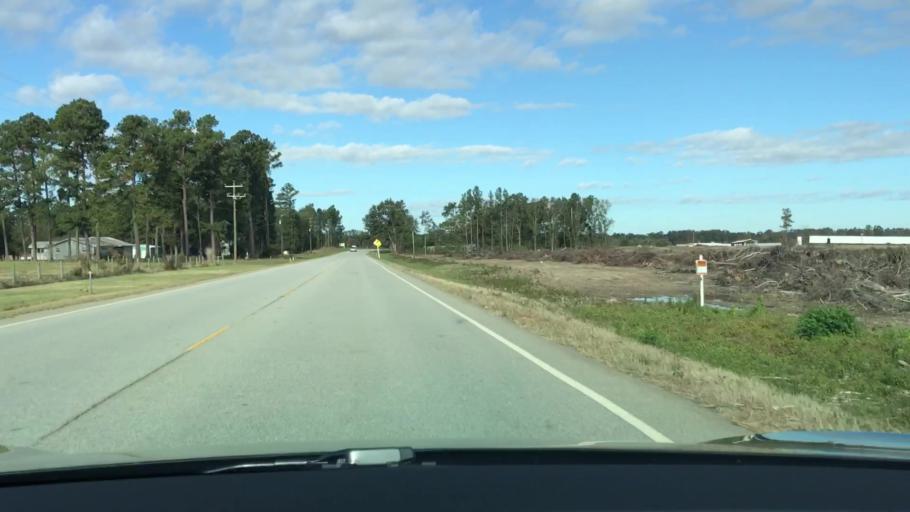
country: US
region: Georgia
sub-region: Jefferson County
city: Wrens
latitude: 33.1216
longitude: -82.4459
